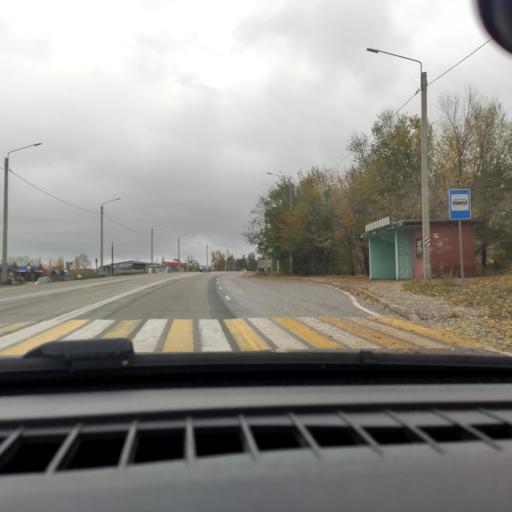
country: RU
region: Voronezj
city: Uryv-Pokrovka
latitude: 51.0435
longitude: 38.9818
